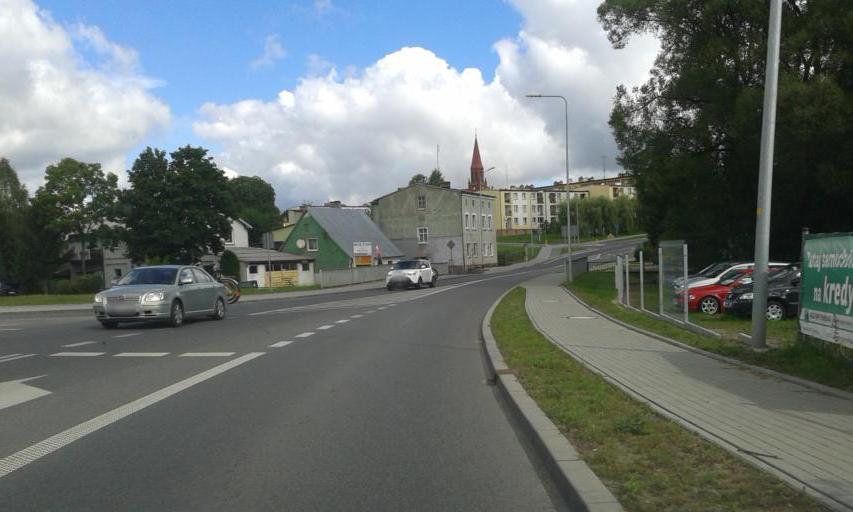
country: PL
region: West Pomeranian Voivodeship
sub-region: Powiat koszalinski
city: Bobolice
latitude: 53.9504
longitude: 16.5862
